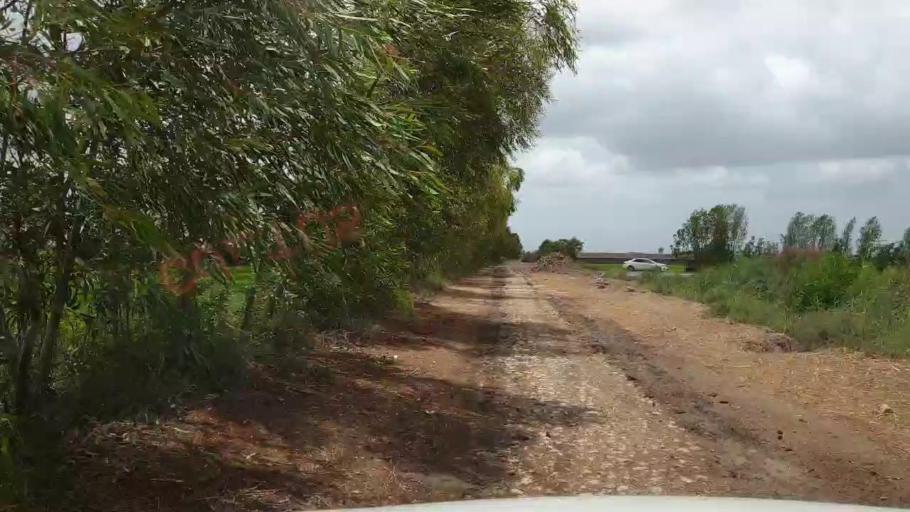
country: PK
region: Sindh
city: Kario
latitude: 24.7431
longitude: 68.5111
